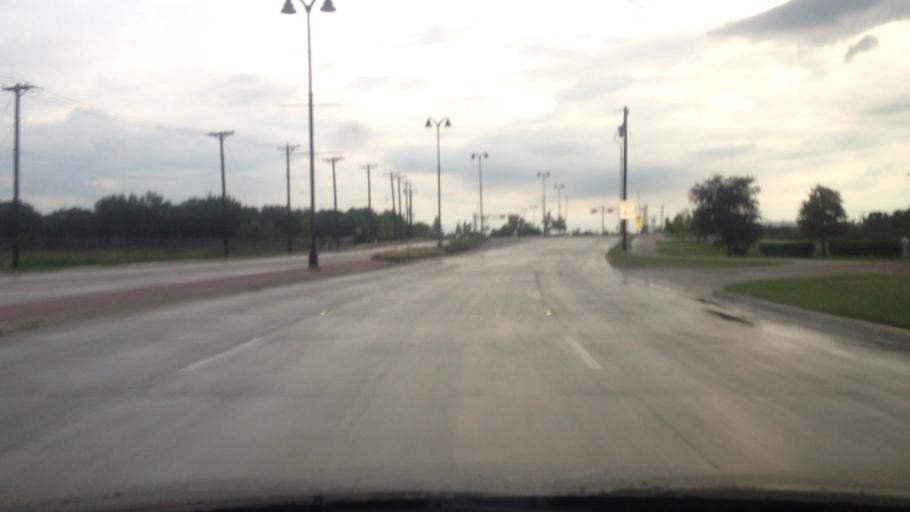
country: US
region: Texas
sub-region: Tarrant County
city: Arlington
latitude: 32.7412
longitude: -97.0836
